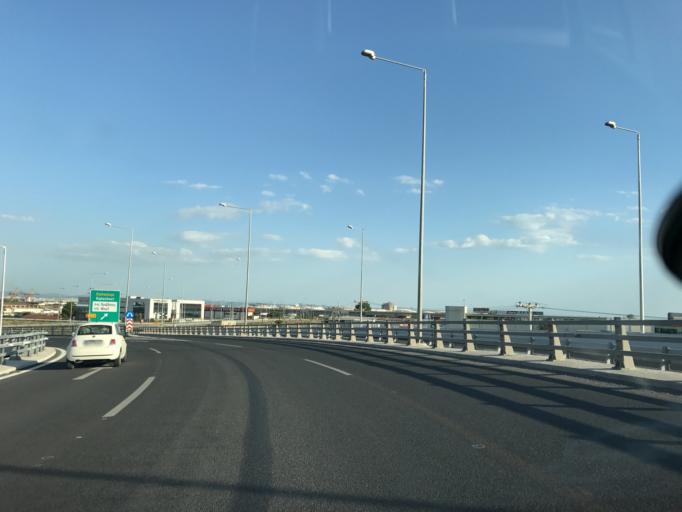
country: GR
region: Central Macedonia
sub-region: Nomos Thessalonikis
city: Menemeni
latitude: 40.6552
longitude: 22.8802
